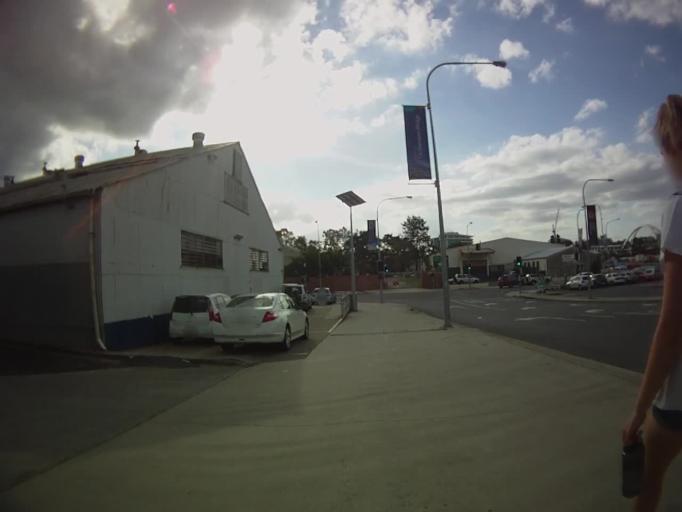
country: AU
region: Queensland
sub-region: Brisbane
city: South Brisbane
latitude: -27.4728
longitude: 153.0135
